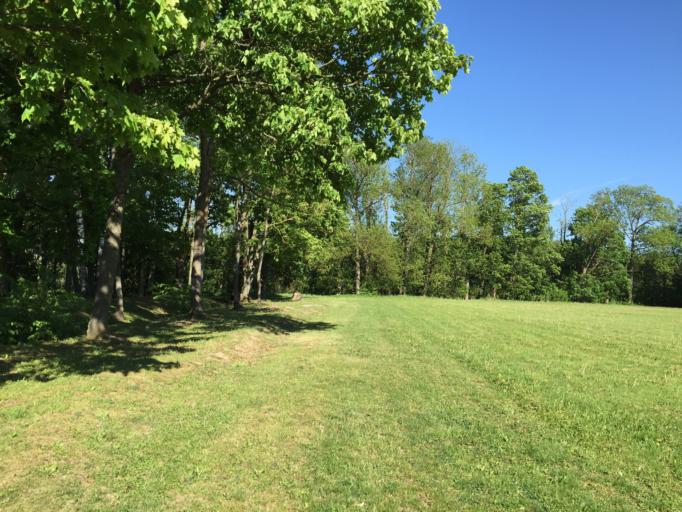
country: LV
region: Jelgava
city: Jelgava
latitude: 56.5209
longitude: 23.7572
